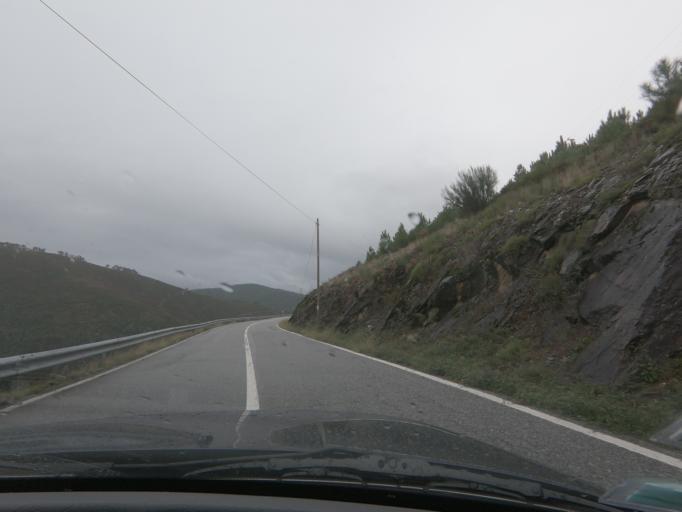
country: PT
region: Vila Real
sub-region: Mondim de Basto
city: Mondim de Basto
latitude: 41.3562
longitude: -7.9159
